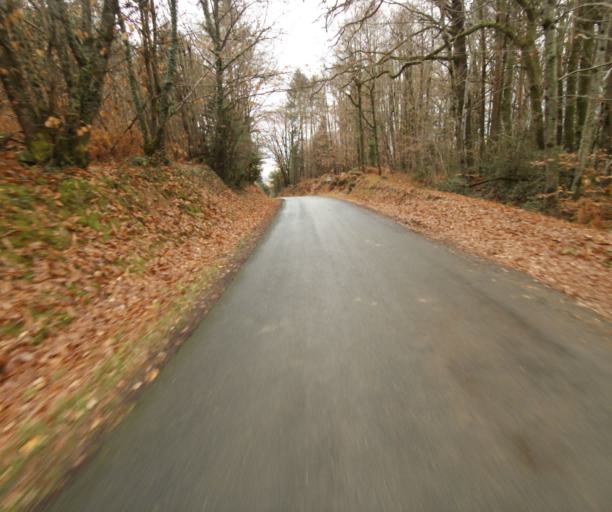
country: FR
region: Limousin
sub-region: Departement de la Correze
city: Saint-Mexant
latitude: 45.2775
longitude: 1.6388
